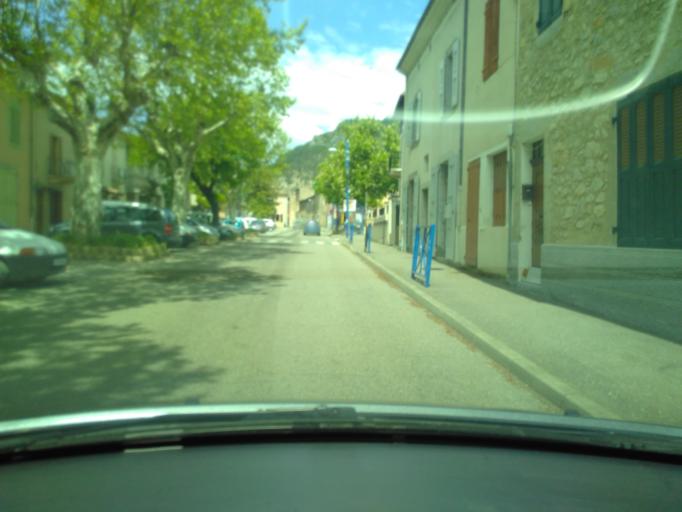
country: FR
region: Rhone-Alpes
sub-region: Departement de la Drome
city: Die
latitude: 44.6131
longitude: 5.4532
